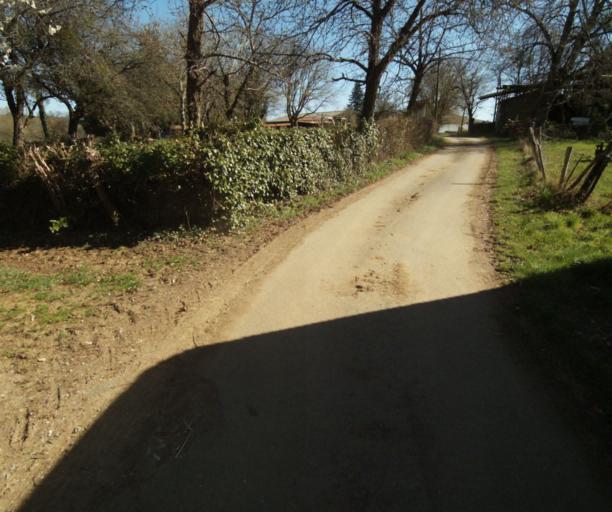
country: FR
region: Limousin
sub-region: Departement de la Correze
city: Chamboulive
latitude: 45.4210
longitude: 1.6618
